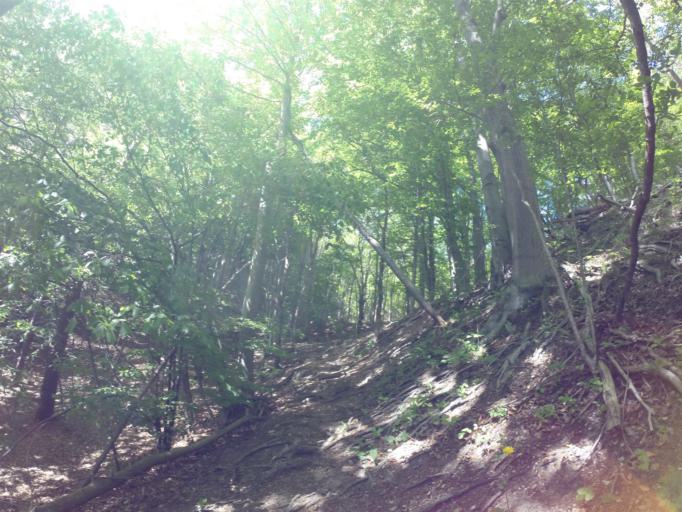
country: DE
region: Thuringia
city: Loberschutz
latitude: 50.9741
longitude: 11.7003
